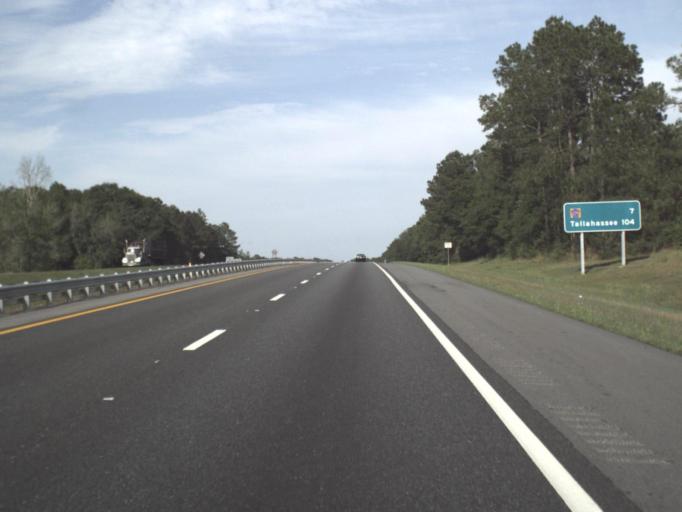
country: US
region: Florida
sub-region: Walton County
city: DeFuniak Springs
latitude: 30.7205
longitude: -85.9191
